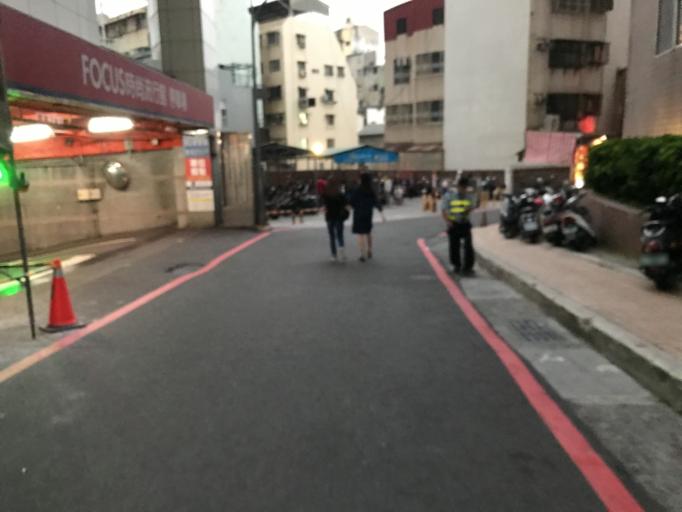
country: TW
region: Taiwan
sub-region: Tainan
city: Tainan
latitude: 22.9955
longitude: 120.2102
